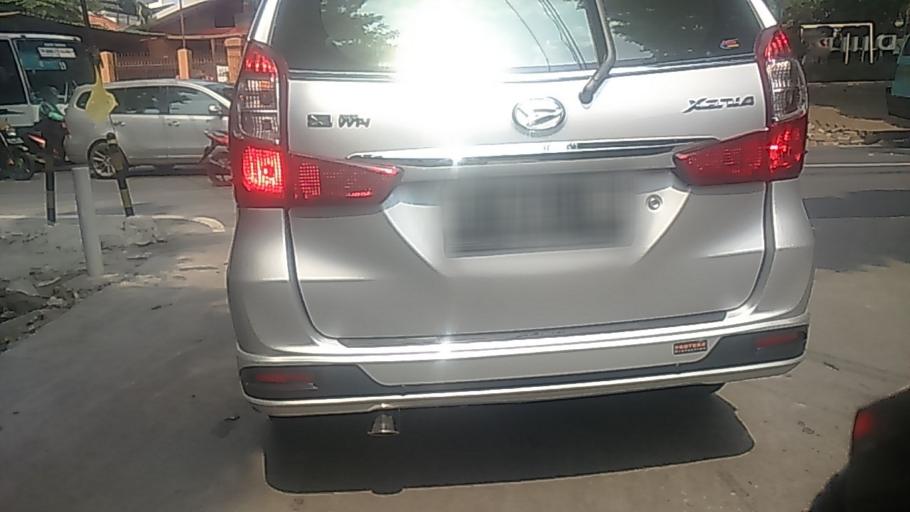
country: ID
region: West Java
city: Depok
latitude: -6.3307
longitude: 106.8075
